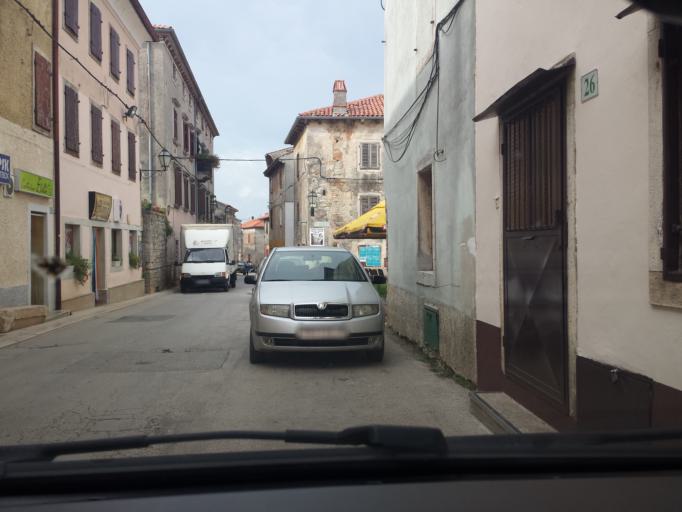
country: HR
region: Istarska
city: Galizana
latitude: 44.9337
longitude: 13.8702
